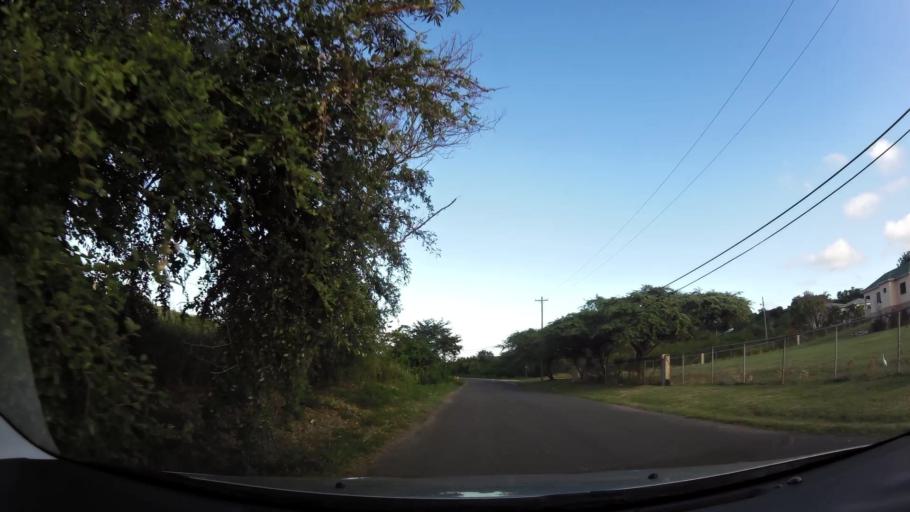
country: AG
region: Saint George
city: Piggotts
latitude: 17.1216
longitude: -61.7971
